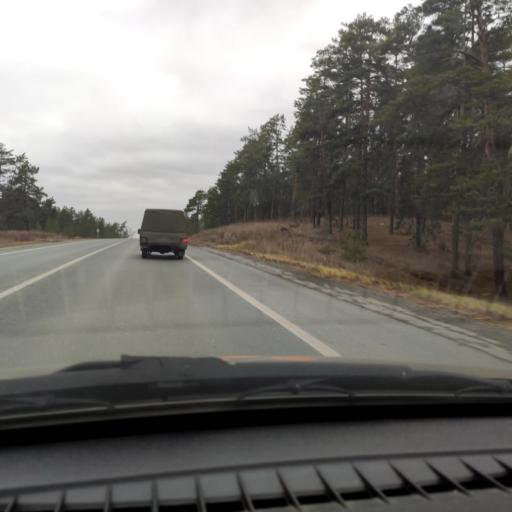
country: RU
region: Samara
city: Volzhskiy
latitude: 53.4424
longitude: 50.1047
